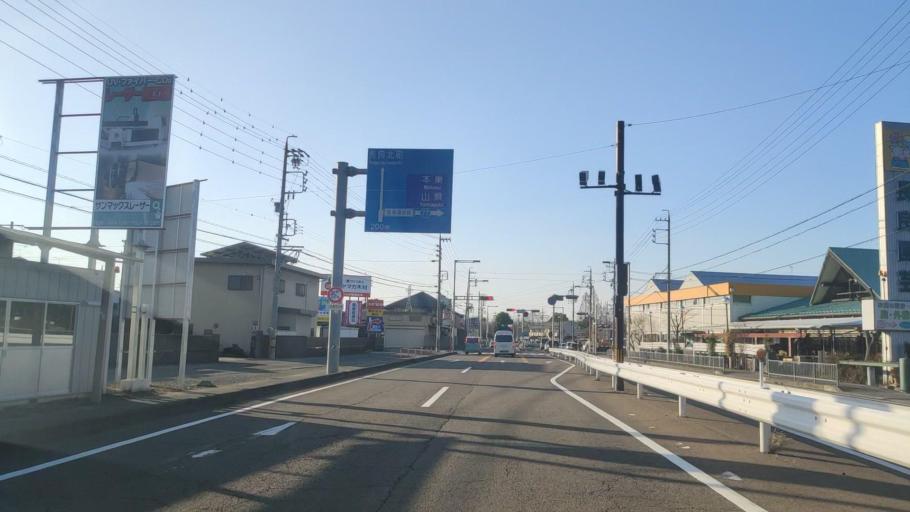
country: JP
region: Gifu
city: Gifu-shi
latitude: 35.4439
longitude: 136.7874
